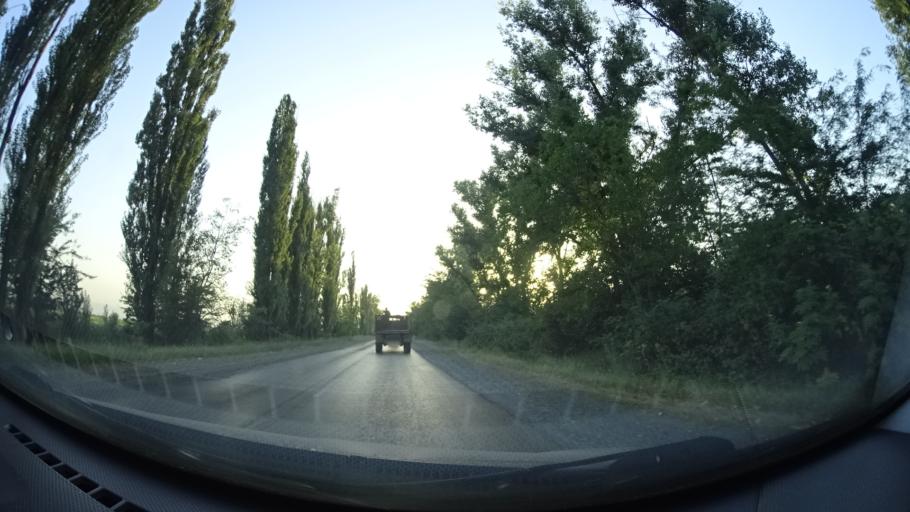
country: GE
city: Bagdadi
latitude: 41.8463
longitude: 46.0712
